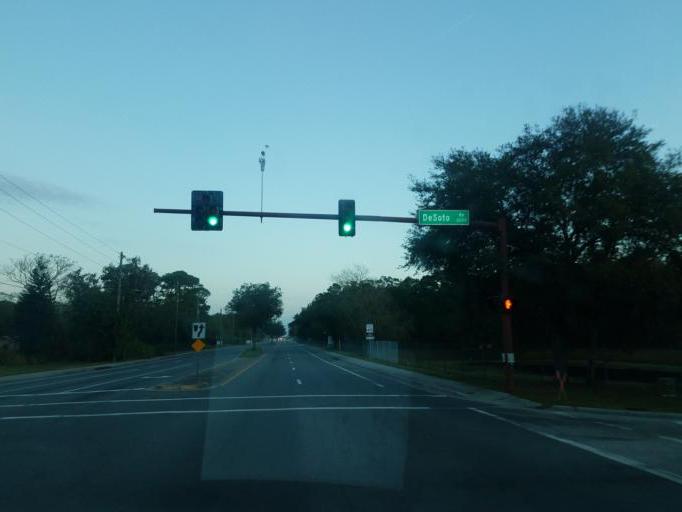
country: US
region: Florida
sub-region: Sarasota County
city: North Sarasota
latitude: 27.3816
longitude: -82.5056
